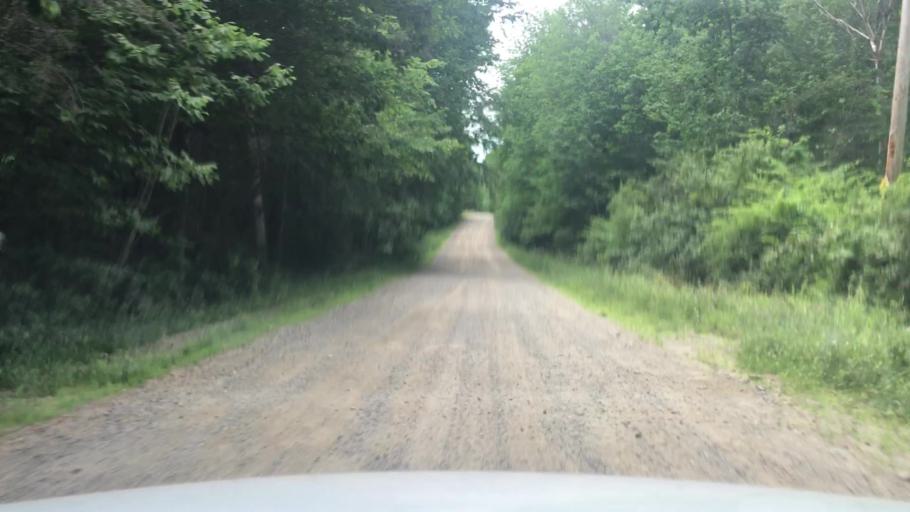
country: US
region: Maine
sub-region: Waldo County
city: Searsmont
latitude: 44.4316
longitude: -69.2545
